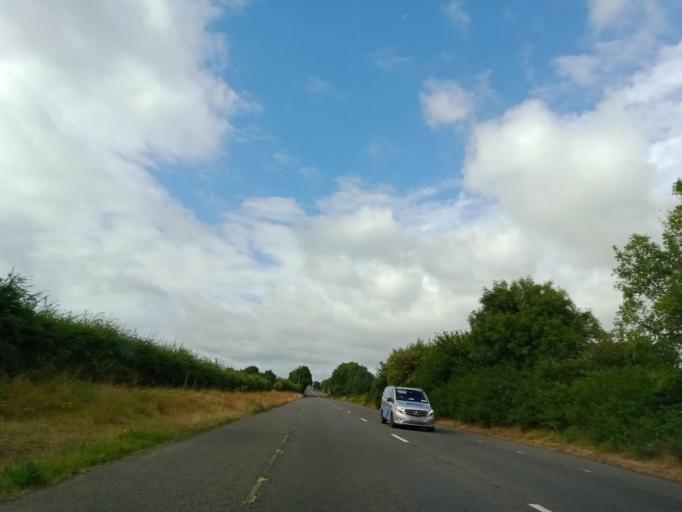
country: IE
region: Leinster
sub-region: Laois
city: Abbeyleix
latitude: 52.8333
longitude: -7.4427
